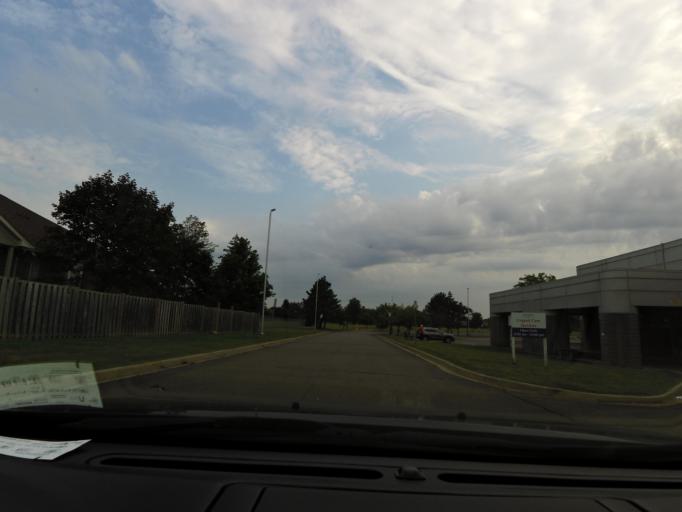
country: CA
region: Ontario
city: Hamilton
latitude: 43.2217
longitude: -79.7748
